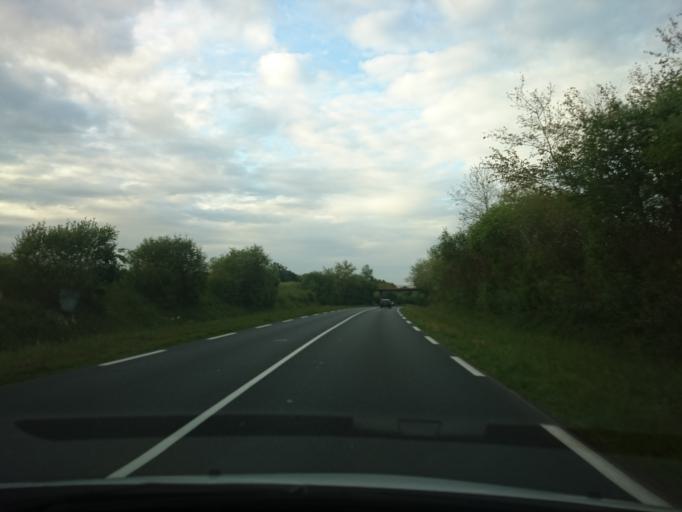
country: FR
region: Pays de la Loire
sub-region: Departement de la Loire-Atlantique
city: Indre
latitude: 47.2091
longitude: -1.6663
